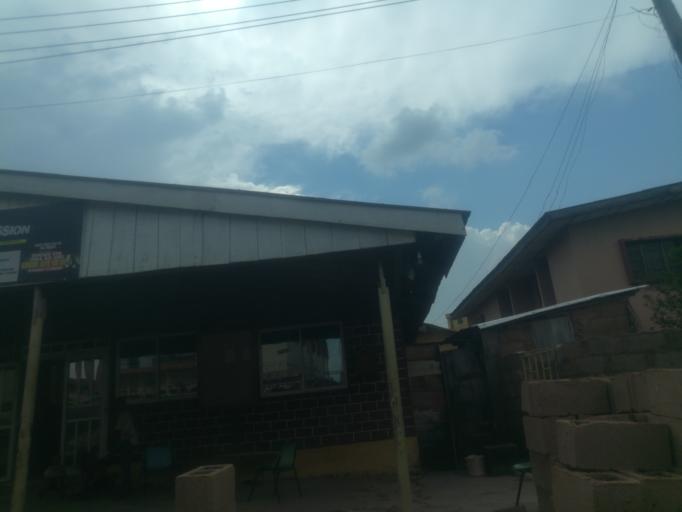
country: NG
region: Oyo
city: Ibadan
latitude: 7.4165
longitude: 3.8971
